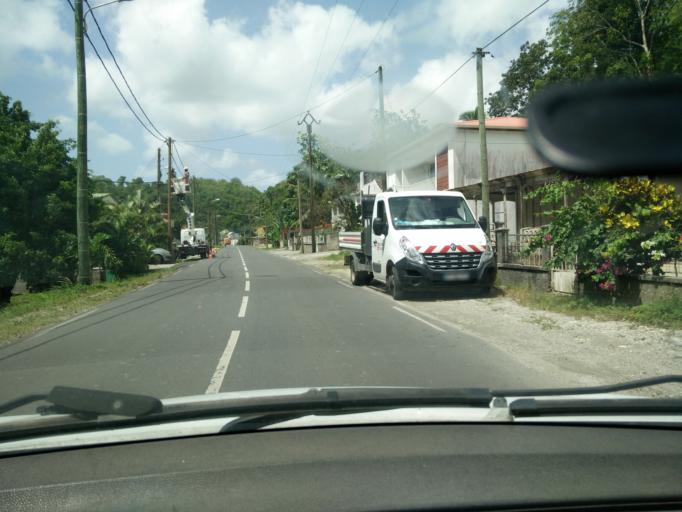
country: GP
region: Guadeloupe
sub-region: Guadeloupe
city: Les Abymes
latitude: 16.2959
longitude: -61.4619
